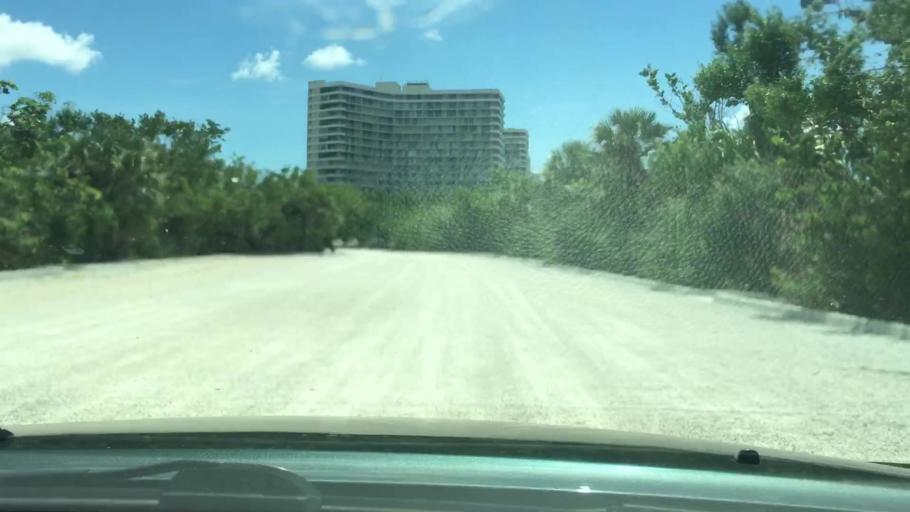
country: US
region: Florida
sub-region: Collier County
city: Marco
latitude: 25.9478
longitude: -81.7420
